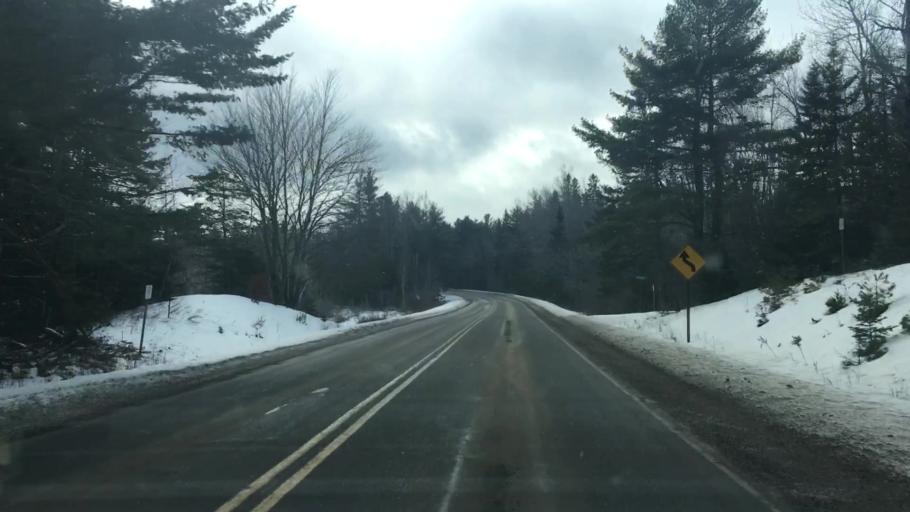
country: US
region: Maine
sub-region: Washington County
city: Calais
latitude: 45.0475
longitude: -67.3272
